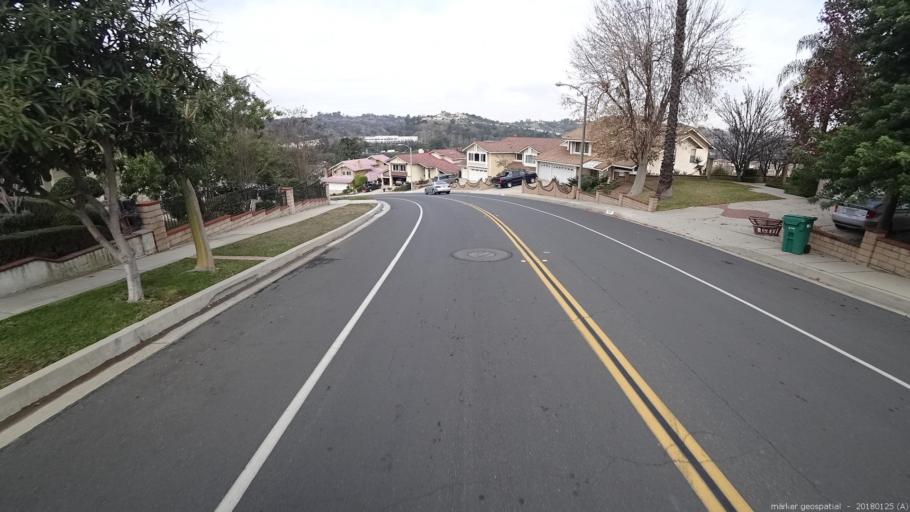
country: US
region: California
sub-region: Los Angeles County
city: Walnut
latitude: 33.9636
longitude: -117.8467
